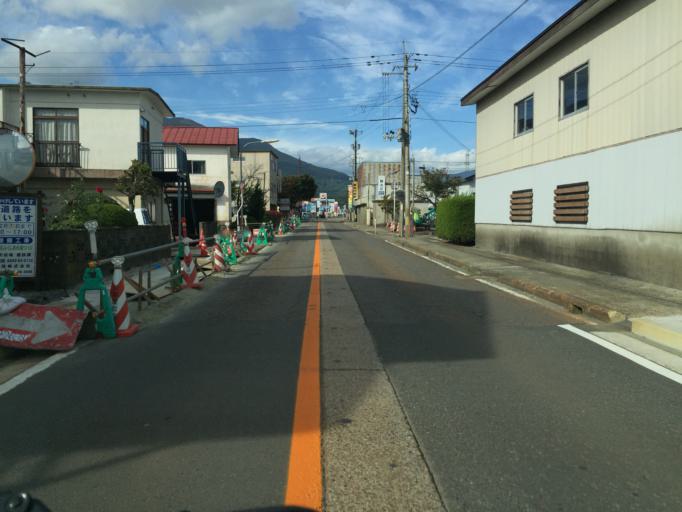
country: JP
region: Fukushima
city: Inawashiro
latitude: 37.5481
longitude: 140.1059
